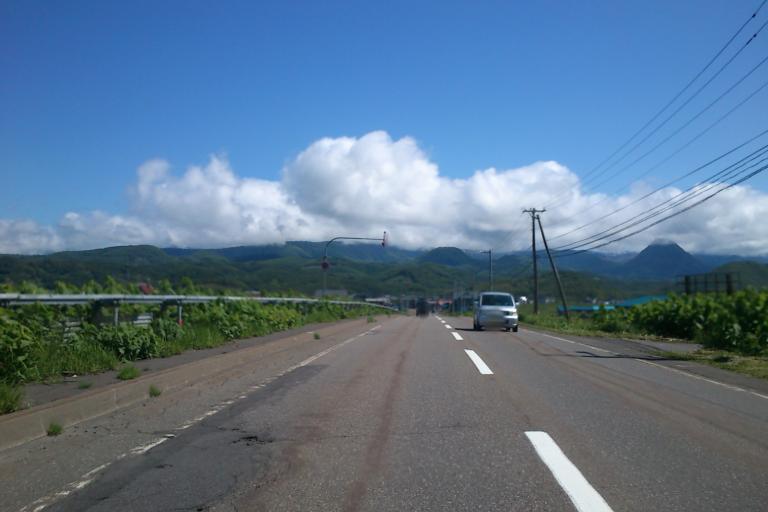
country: JP
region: Hokkaido
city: Ishikari
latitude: 43.5709
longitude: 141.3823
